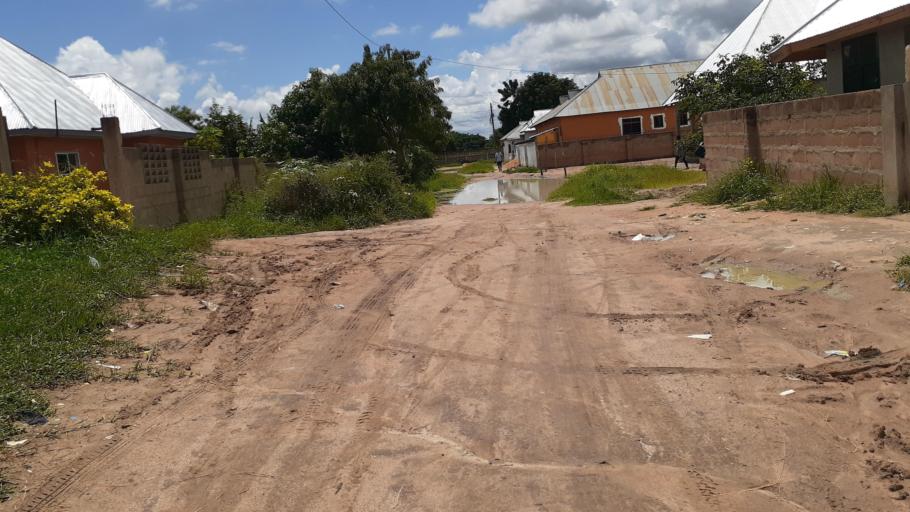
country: TZ
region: Dodoma
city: Dodoma
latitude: -6.1190
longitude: 35.7434
